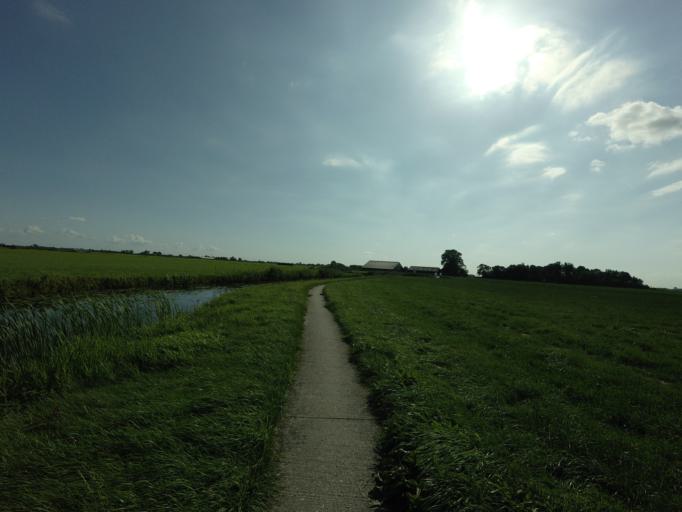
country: NL
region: Friesland
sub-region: Gemeente Littenseradiel
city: Makkum
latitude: 53.0919
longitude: 5.6368
